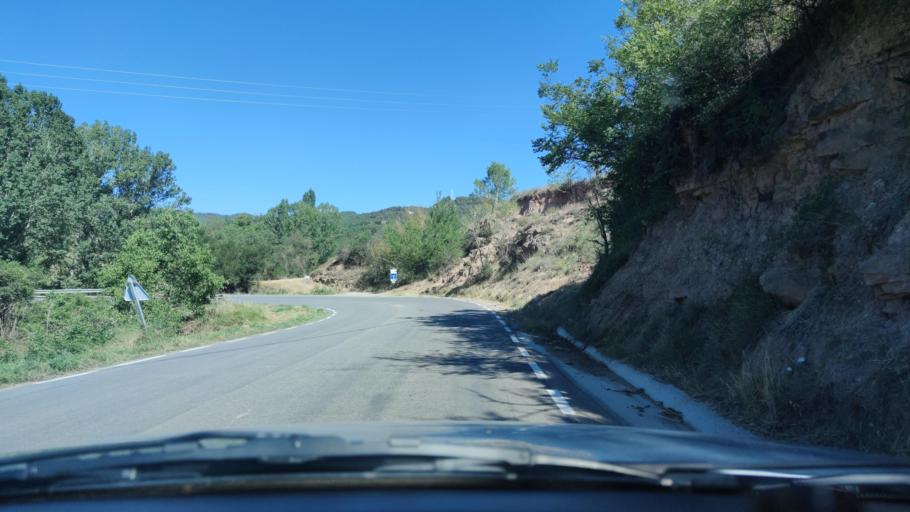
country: ES
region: Catalonia
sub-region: Provincia de Lleida
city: Solsona
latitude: 41.9861
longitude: 1.5052
